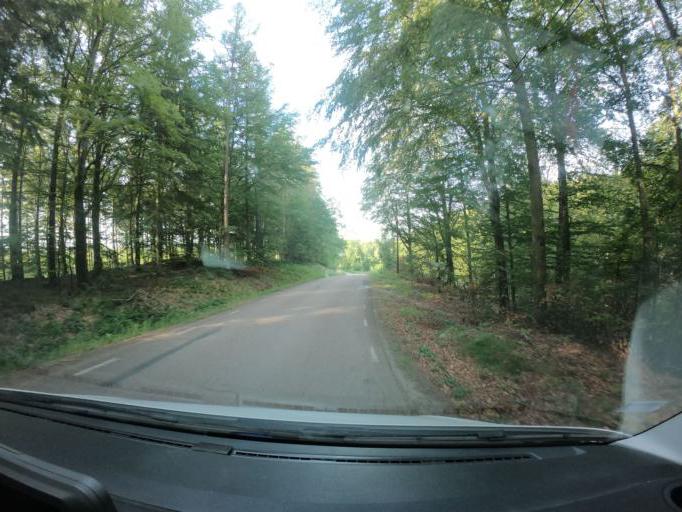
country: SE
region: Skane
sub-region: Angelholms Kommun
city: Munka-Ljungby
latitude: 56.3261
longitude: 13.0933
